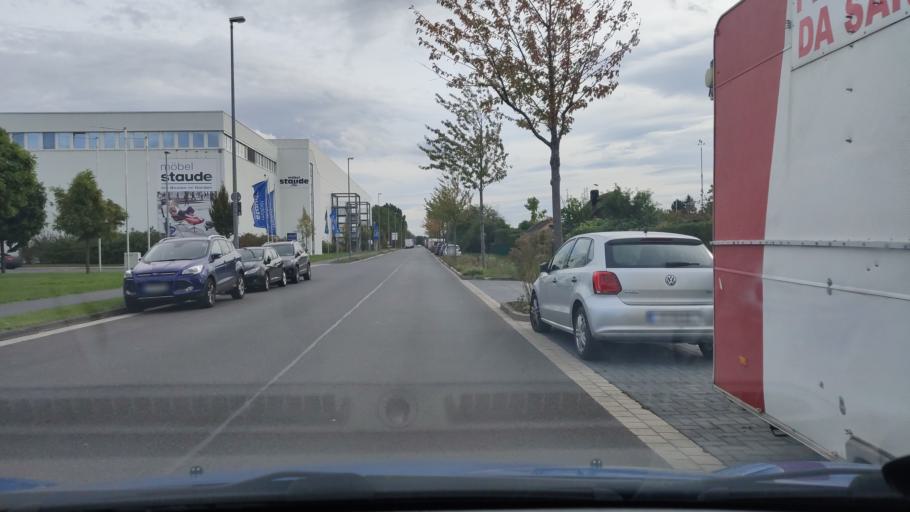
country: DE
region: Lower Saxony
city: Hannover
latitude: 52.4071
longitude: 9.7028
